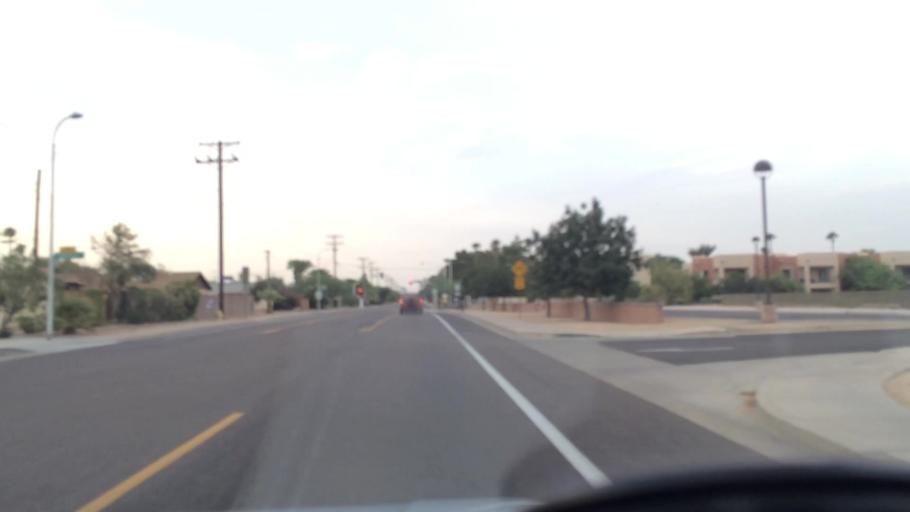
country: US
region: Arizona
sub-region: Maricopa County
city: Tempe
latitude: 33.4569
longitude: -111.9178
